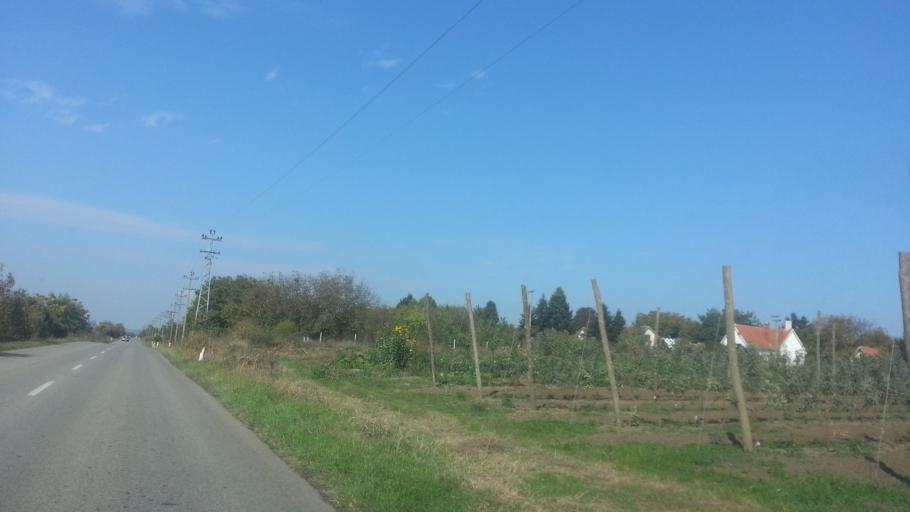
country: RS
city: Surduk
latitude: 45.0870
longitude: 20.3040
